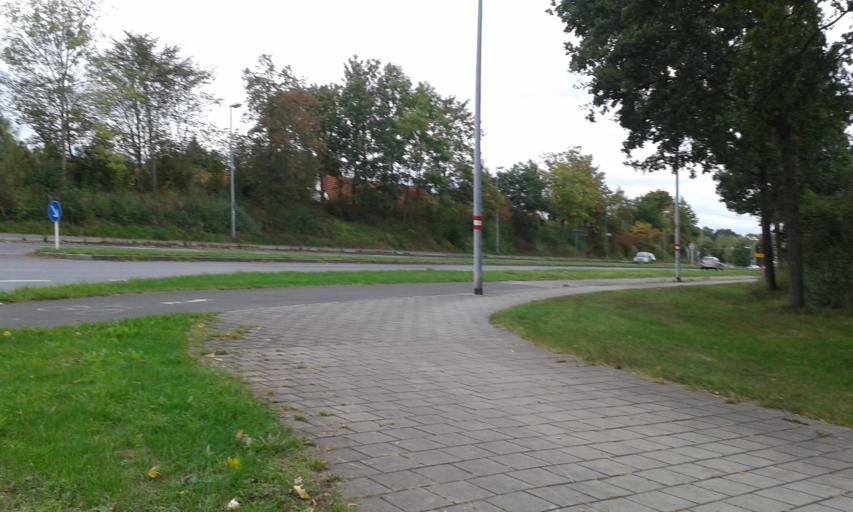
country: DE
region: Bavaria
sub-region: Upper Franconia
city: Bamberg
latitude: 49.8717
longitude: 10.8904
